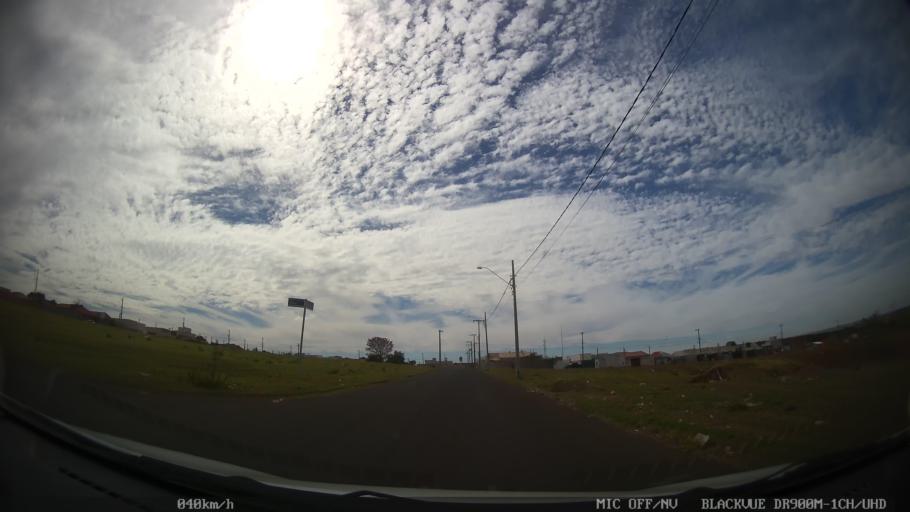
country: BR
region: Sao Paulo
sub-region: Catanduva
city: Catanduva
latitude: -21.1690
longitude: -48.9677
